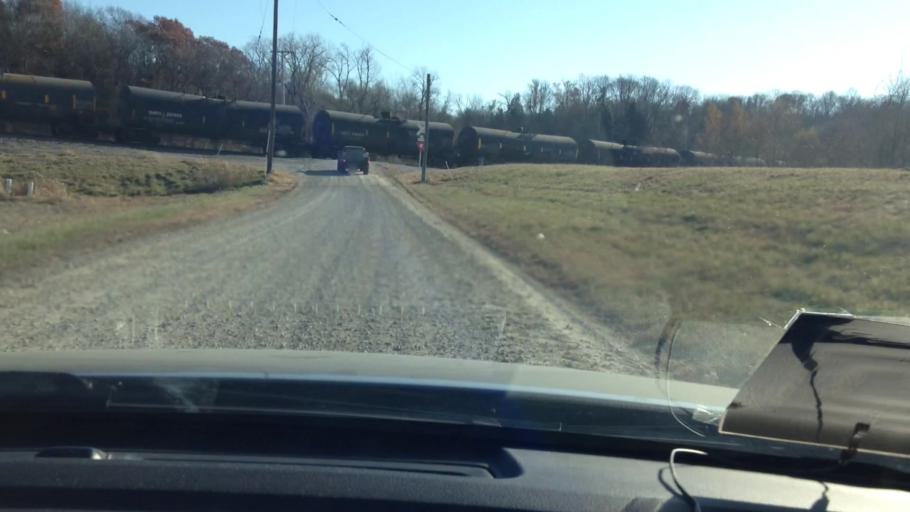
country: US
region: Kansas
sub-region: Leavenworth County
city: Leavenworth
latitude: 39.3280
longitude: -94.8585
